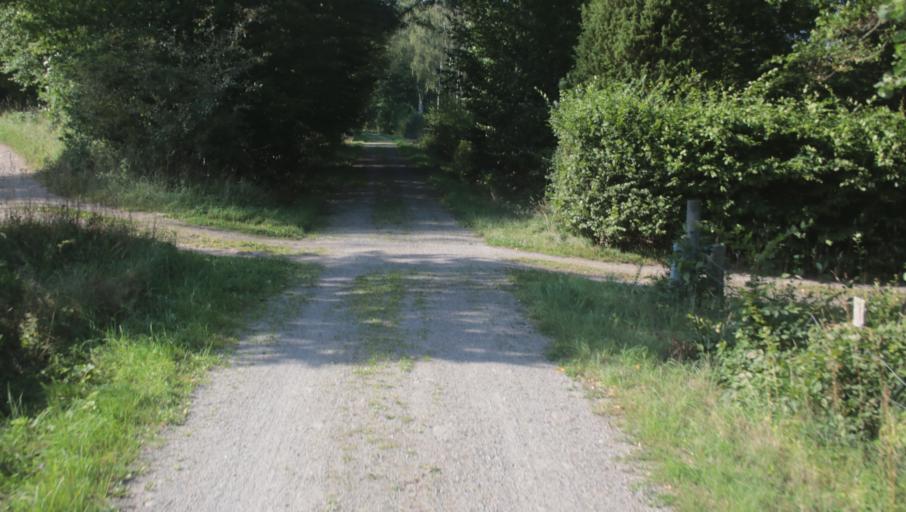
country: SE
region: Blekinge
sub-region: Karlshamns Kommun
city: Svangsta
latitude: 56.2934
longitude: 14.7418
